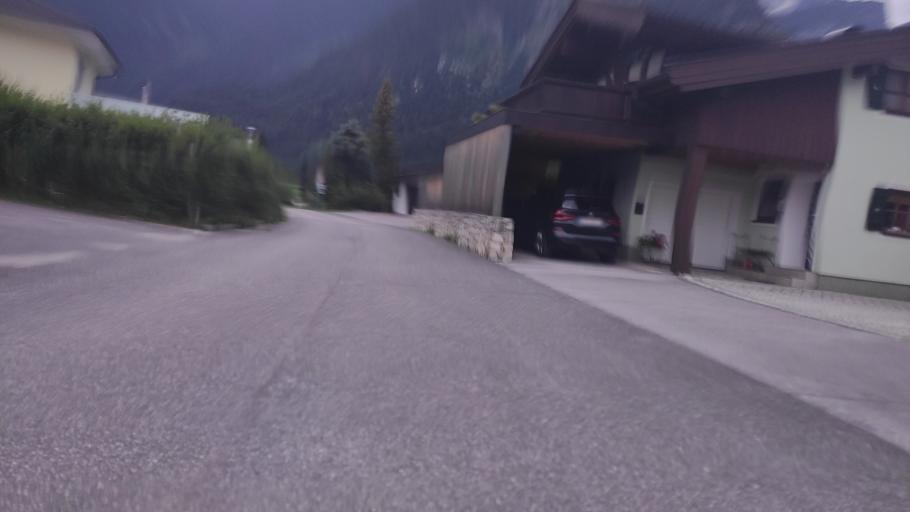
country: AT
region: Salzburg
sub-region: Politischer Bezirk Zell am See
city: Lofer
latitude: 47.5810
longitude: 12.6913
